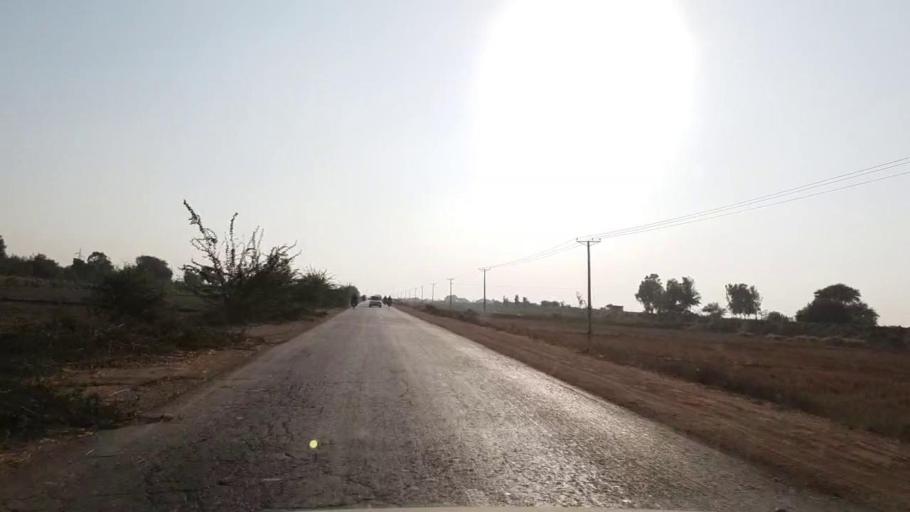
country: PK
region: Sindh
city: Mirpur Batoro
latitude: 24.7635
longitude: 68.2756
